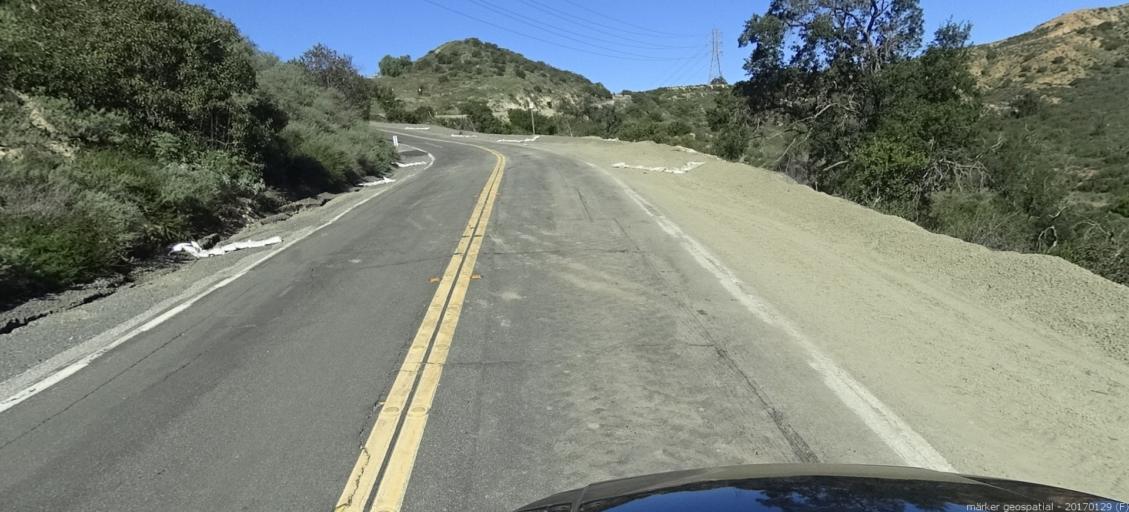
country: US
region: California
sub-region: Orange County
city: Portola Hills
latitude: 33.6994
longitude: -117.6345
